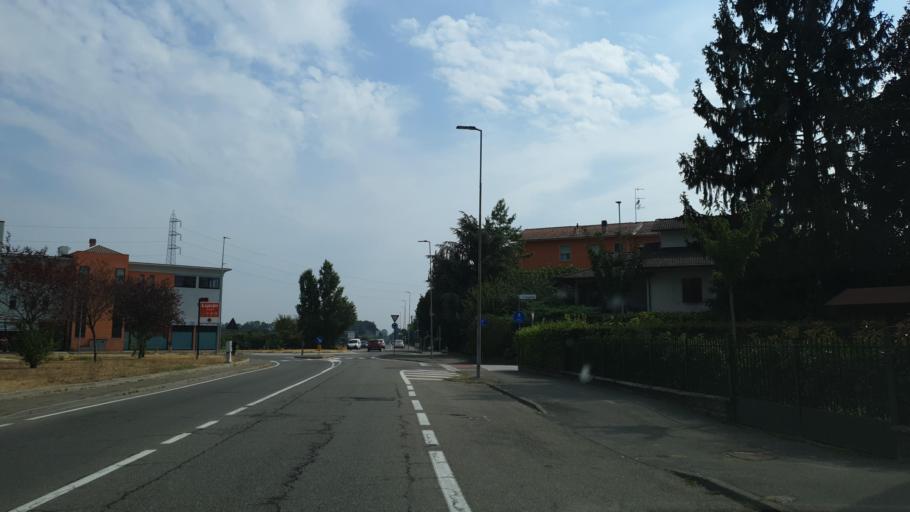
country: IT
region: Emilia-Romagna
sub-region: Provincia di Parma
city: Baganzola
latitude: 44.8223
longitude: 10.2825
